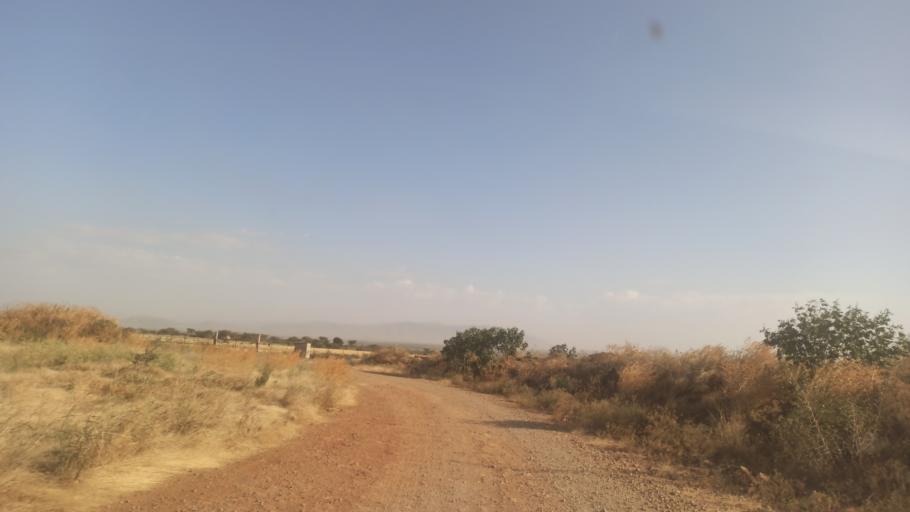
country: ET
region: Oromiya
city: Ziway
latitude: 7.9343
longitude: 38.6208
